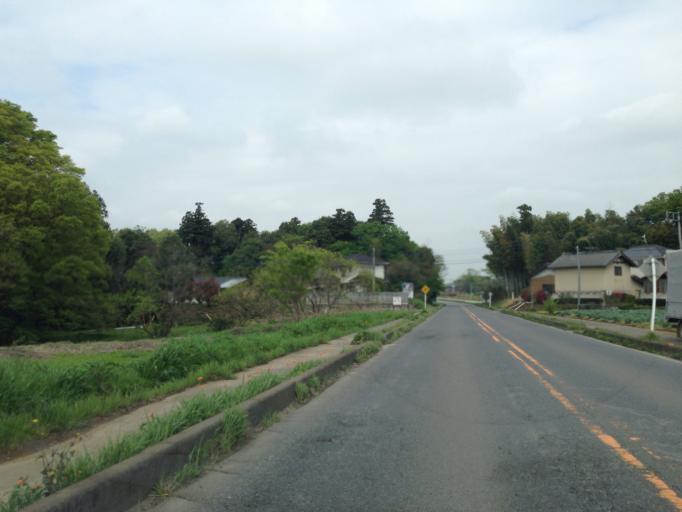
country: JP
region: Ibaraki
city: Sakai
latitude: 36.1697
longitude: 139.8455
